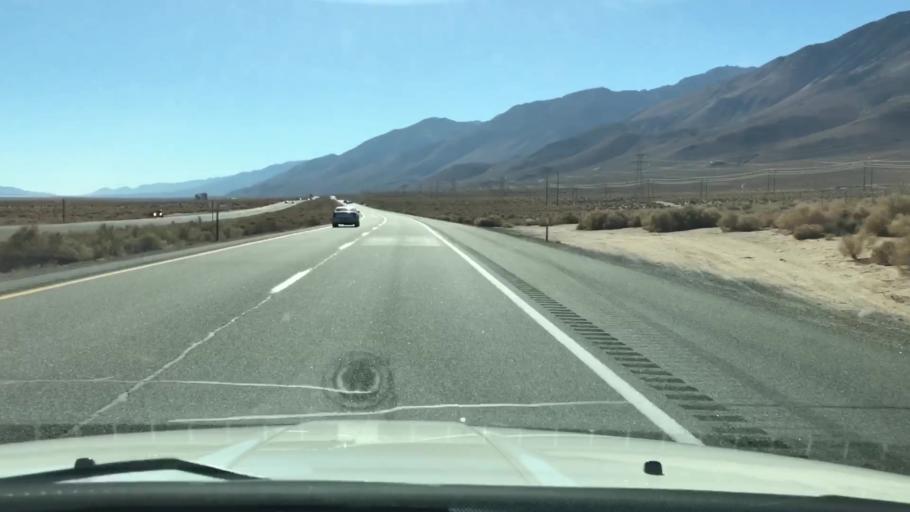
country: US
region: California
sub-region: Inyo County
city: Lone Pine
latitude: 36.5009
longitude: -118.0327
